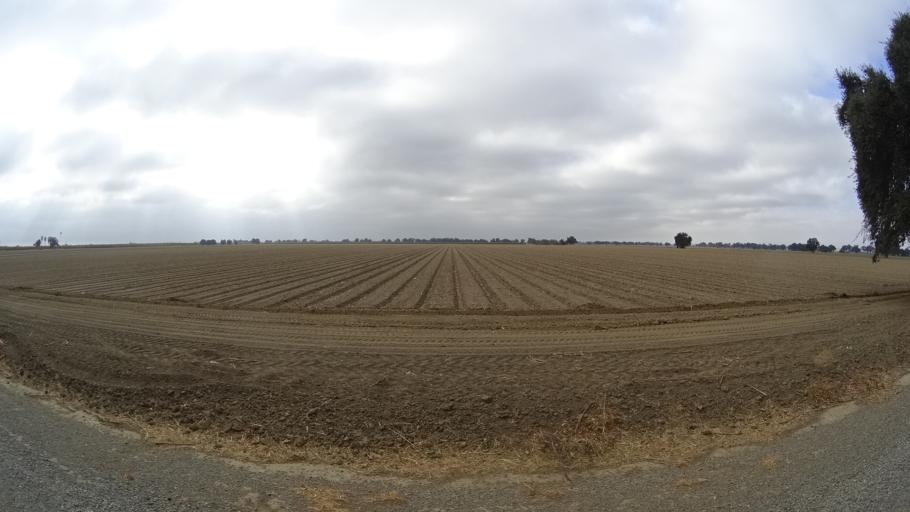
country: US
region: California
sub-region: Yolo County
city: Woodland
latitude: 38.7936
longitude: -121.8284
